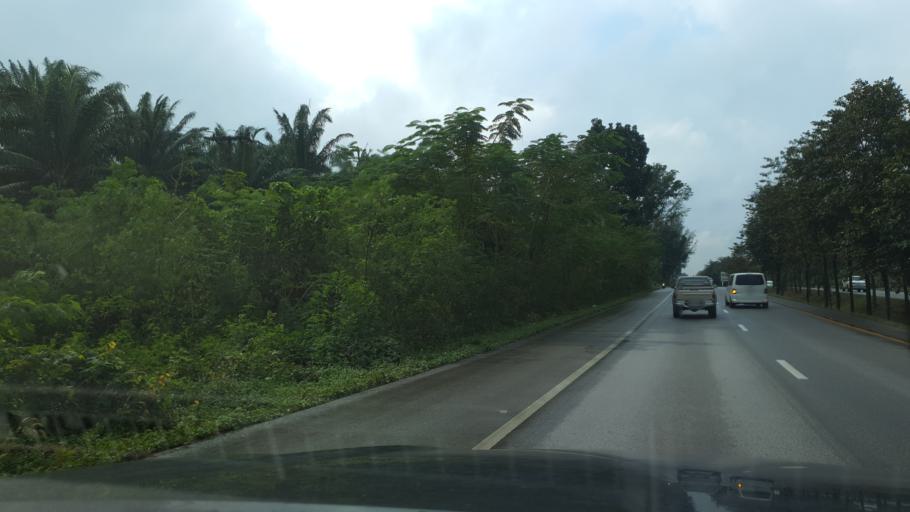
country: TH
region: Prachuap Khiri Khan
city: Bang Saphan Noi
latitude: 10.9423
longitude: 99.2962
